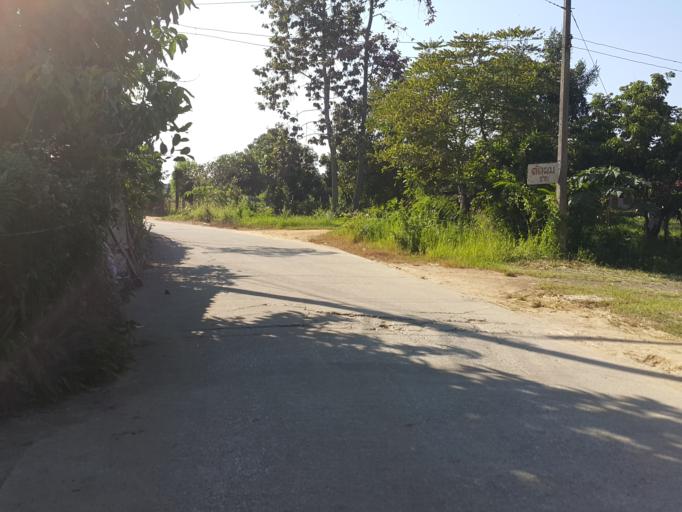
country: TH
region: Chiang Mai
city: Mae On
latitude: 18.8005
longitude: 99.1832
